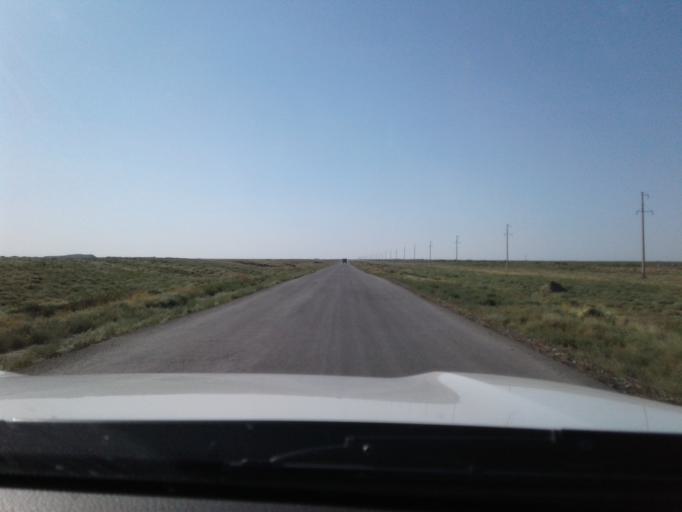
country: IR
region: Razavi Khorasan
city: Kalat-e Naderi
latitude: 37.1374
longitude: 60.0742
